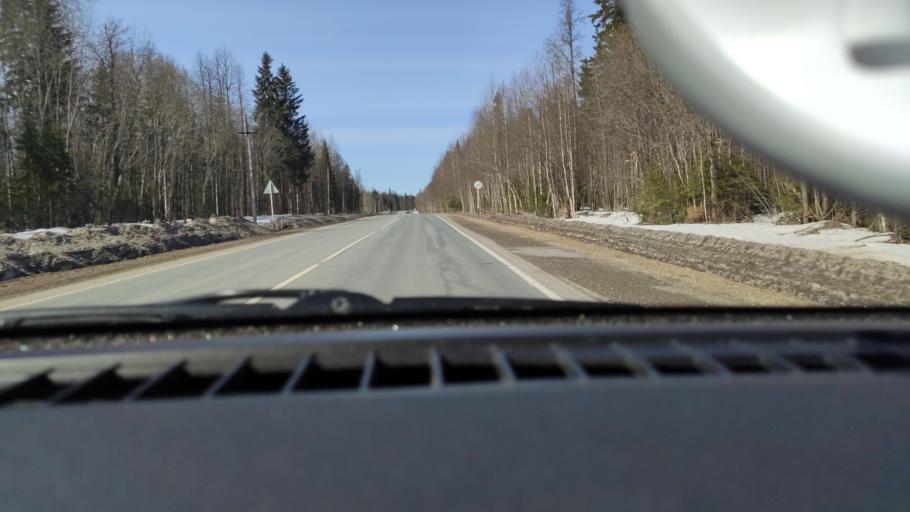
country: RU
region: Perm
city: Perm
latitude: 58.2101
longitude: 56.1889
